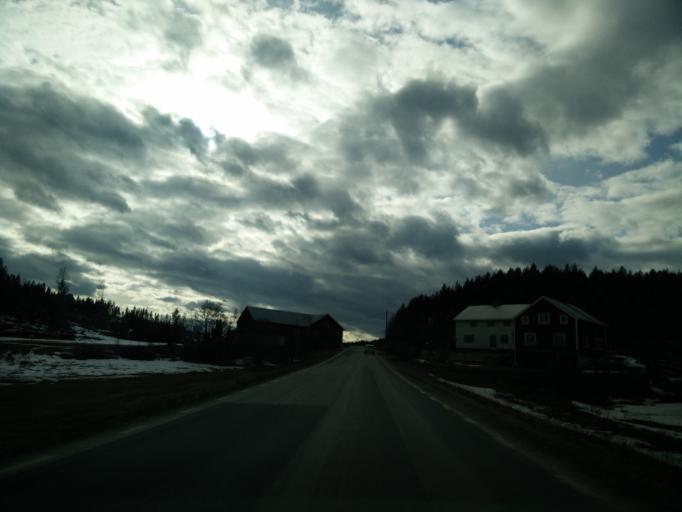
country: SE
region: Vaesternorrland
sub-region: Haernoesands Kommun
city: Haernoesand
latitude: 62.6829
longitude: 17.8893
